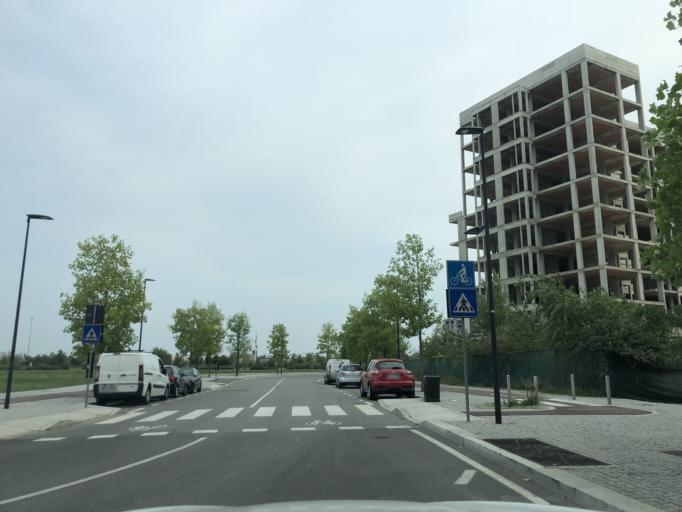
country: IT
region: Lombardy
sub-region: Citta metropolitana di Milano
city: Pero
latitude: 45.5118
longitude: 9.1008
